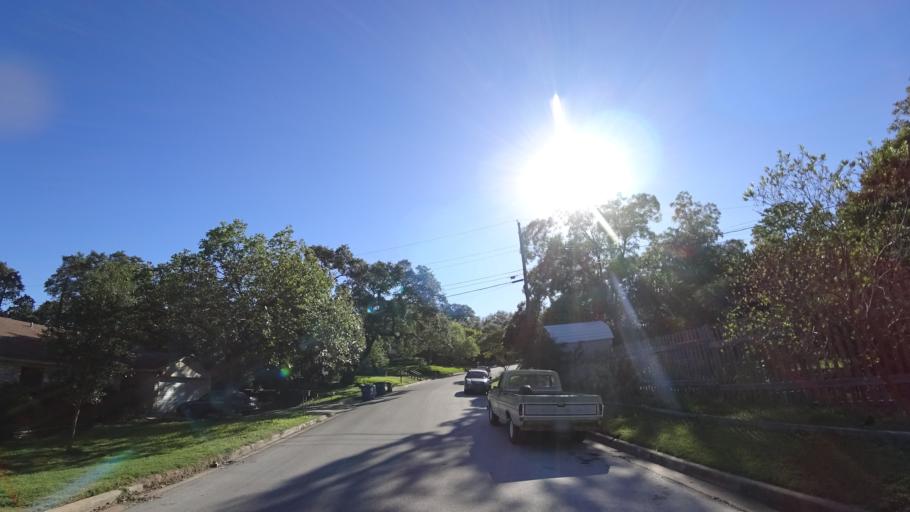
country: US
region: Texas
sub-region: Travis County
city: Rollingwood
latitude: 30.2366
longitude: -97.8064
